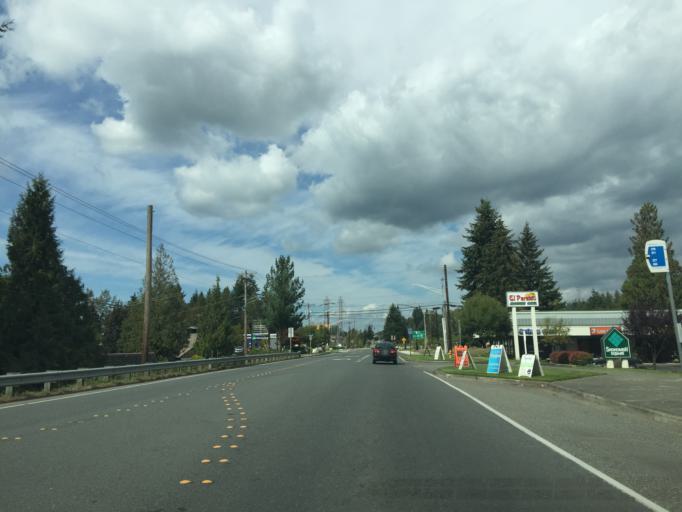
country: US
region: Washington
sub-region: Snohomish County
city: Snohomish
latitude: 47.9284
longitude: -122.0991
